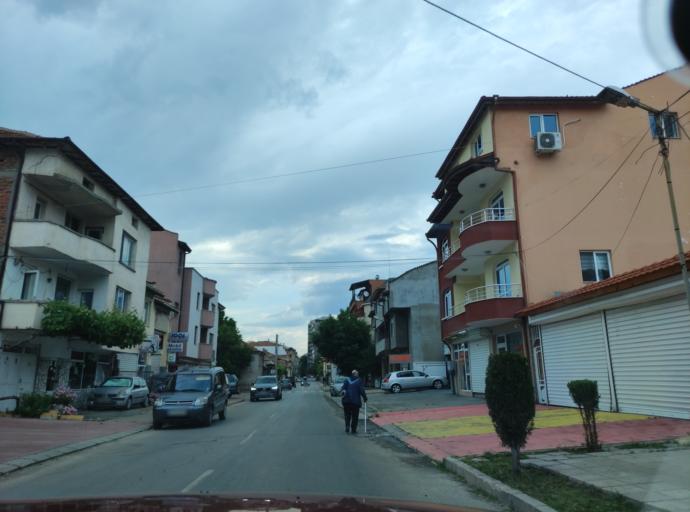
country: BG
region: Pazardzhik
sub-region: Obshtina Pazardzhik
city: Pazardzhik
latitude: 42.1834
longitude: 24.3350
